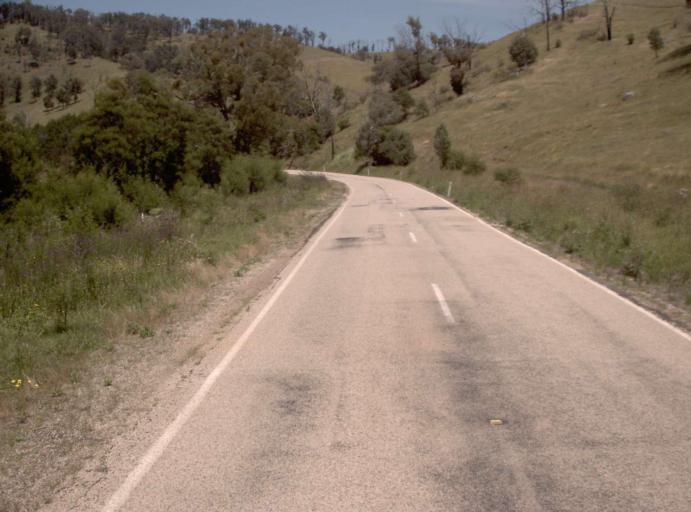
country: AU
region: Victoria
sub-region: East Gippsland
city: Bairnsdale
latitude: -37.5233
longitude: 147.8460
